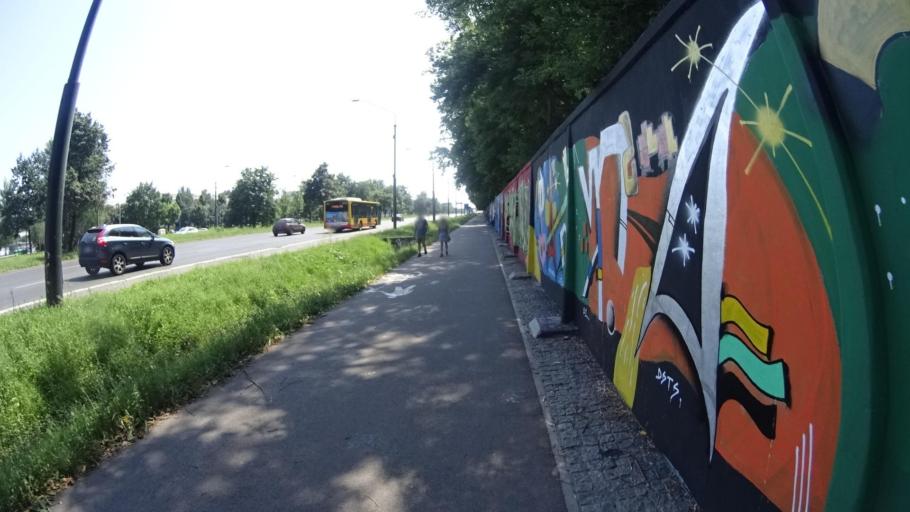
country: PL
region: Masovian Voivodeship
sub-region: Warszawa
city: Ursynow
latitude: 52.1595
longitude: 21.0169
